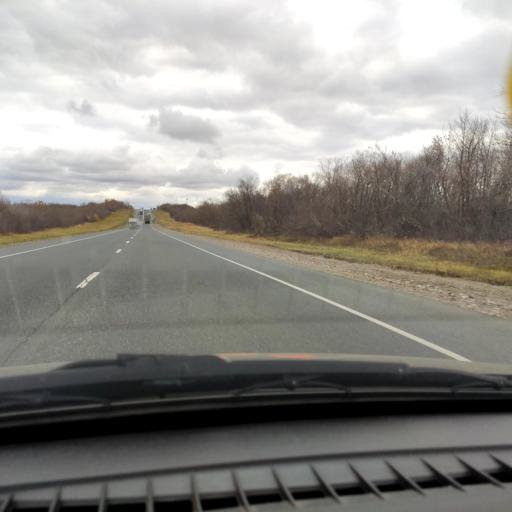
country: RU
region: Samara
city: Mezhdurechensk
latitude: 53.2573
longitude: 49.1147
